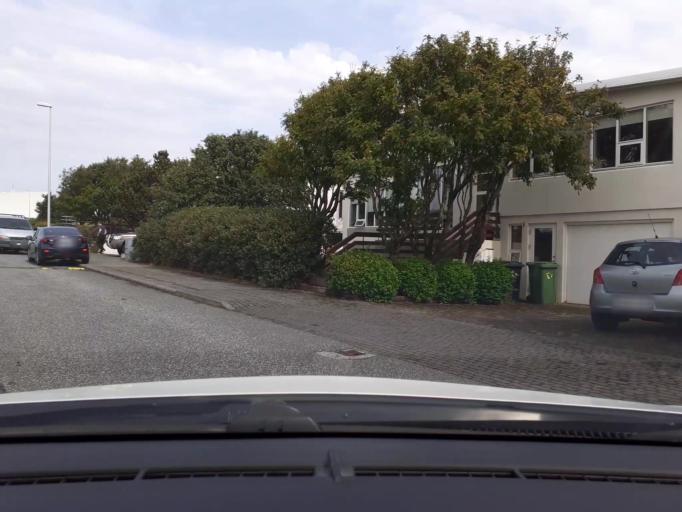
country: IS
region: Southern Peninsula
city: Reykjanesbaer
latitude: 63.9882
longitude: -22.5507
